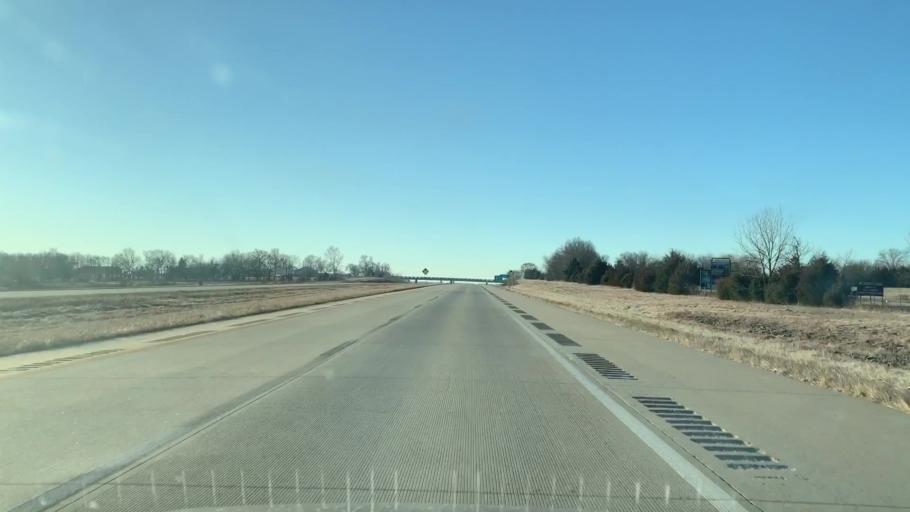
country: US
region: Kansas
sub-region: Bourbon County
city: Fort Scott
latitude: 37.8683
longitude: -94.7046
